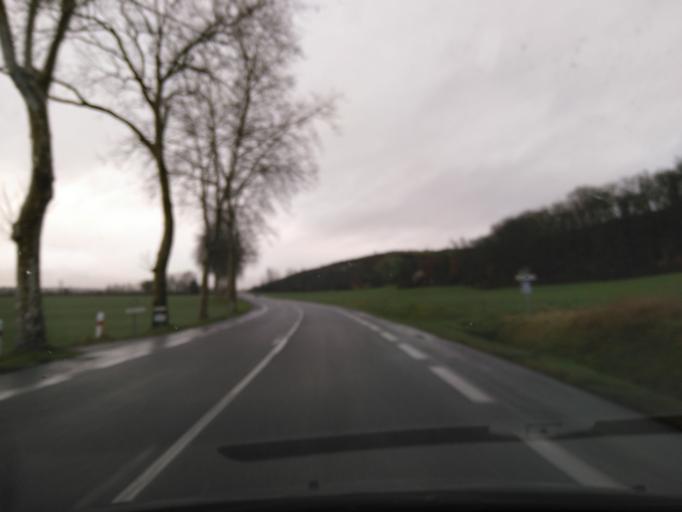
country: FR
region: Midi-Pyrenees
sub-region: Departement de la Haute-Garonne
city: Rieux-Volvestre
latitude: 43.2329
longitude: 1.2080
